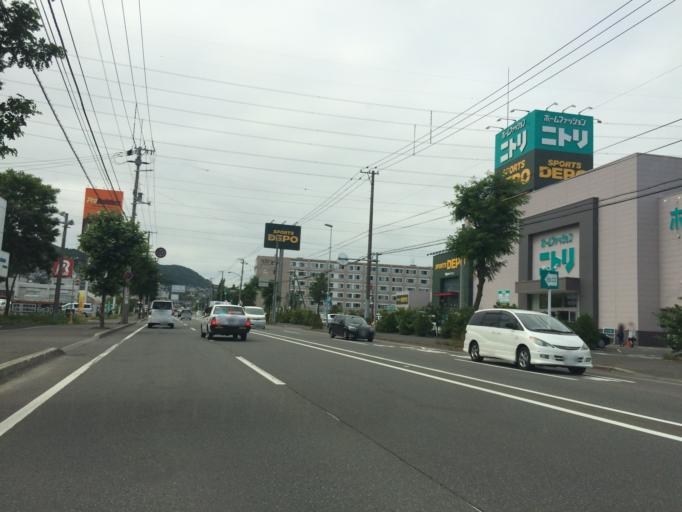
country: JP
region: Hokkaido
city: Sapporo
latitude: 43.0964
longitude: 141.2592
